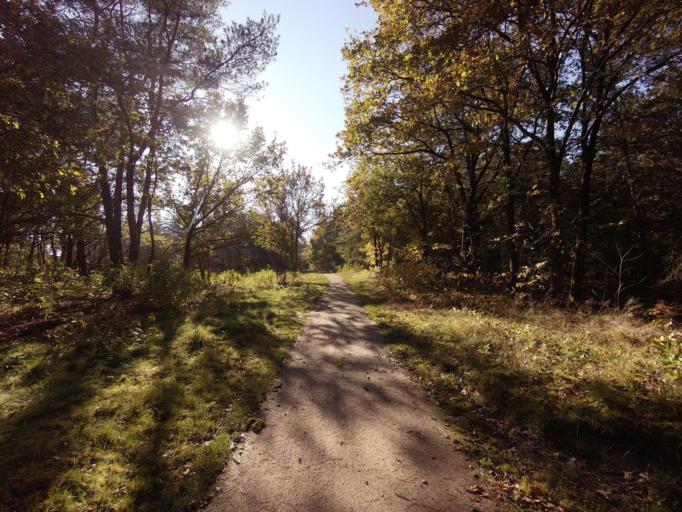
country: NL
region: North Holland
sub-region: Gemeente Laren
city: Laren
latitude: 52.2429
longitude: 5.2275
